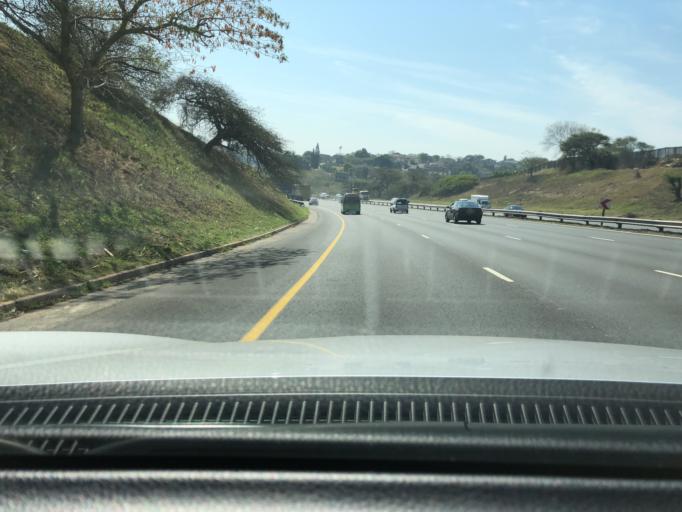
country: ZA
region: KwaZulu-Natal
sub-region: eThekwini Metropolitan Municipality
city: Berea
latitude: -29.8267
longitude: 30.9662
